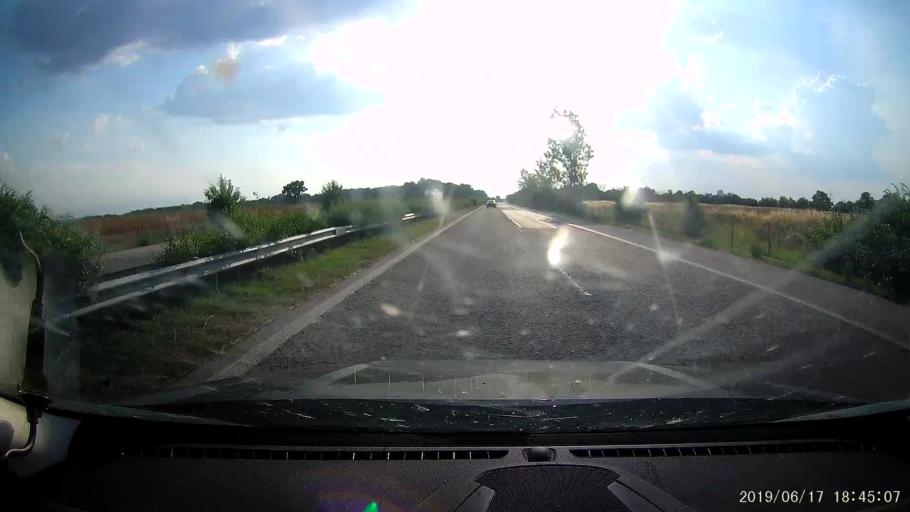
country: BG
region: Stara Zagora
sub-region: Obshtina Chirpan
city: Chirpan
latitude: 42.1938
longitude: 25.1600
